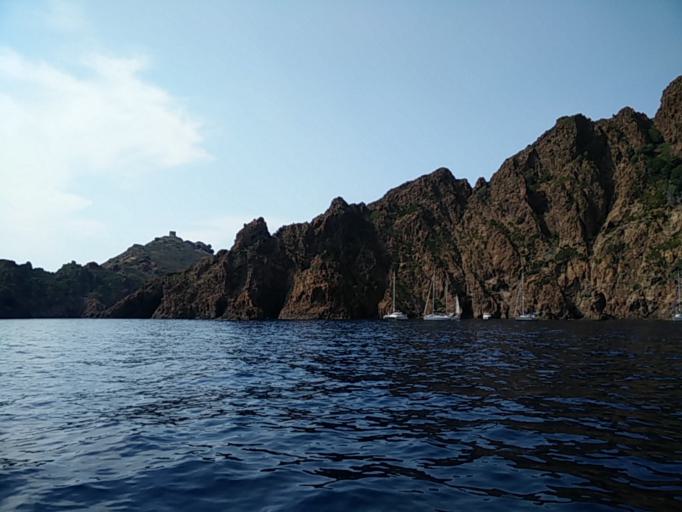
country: FR
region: Corsica
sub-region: Departement de la Corse-du-Sud
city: Cargese
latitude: 42.3651
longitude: 8.5476
